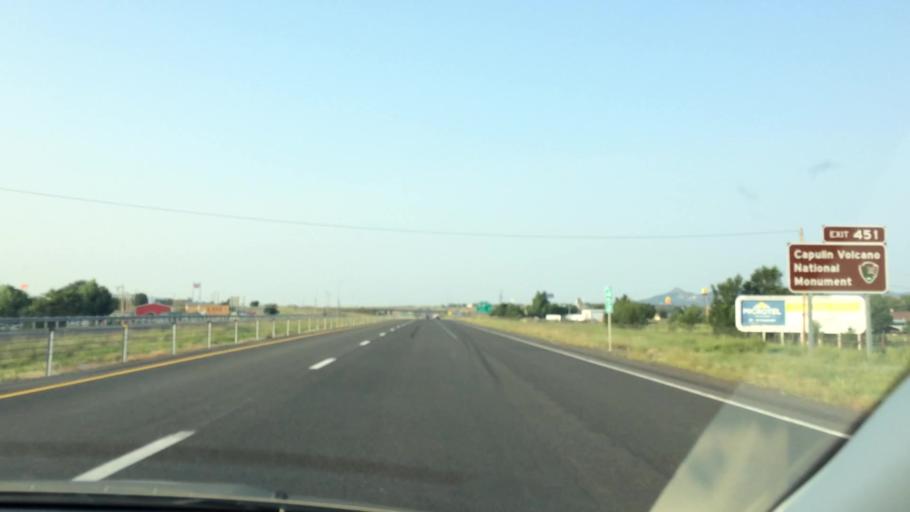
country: US
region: New Mexico
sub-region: Colfax County
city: Raton
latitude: 36.8912
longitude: -104.4287
